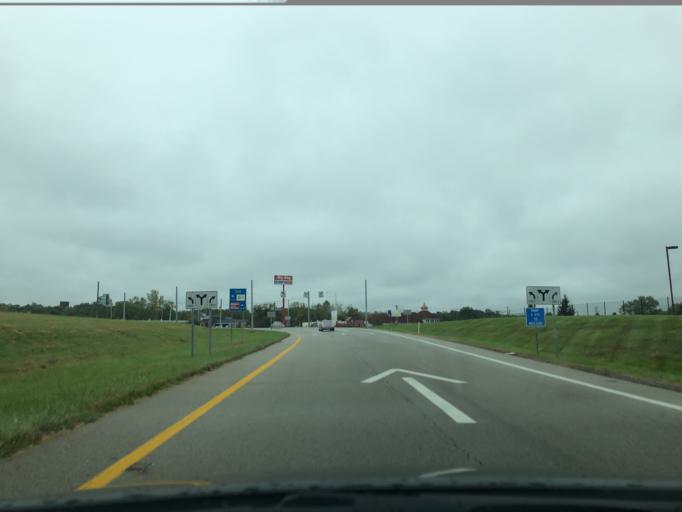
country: US
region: Ohio
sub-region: Hamilton County
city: The Village of Indian Hill
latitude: 39.2262
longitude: -84.2816
